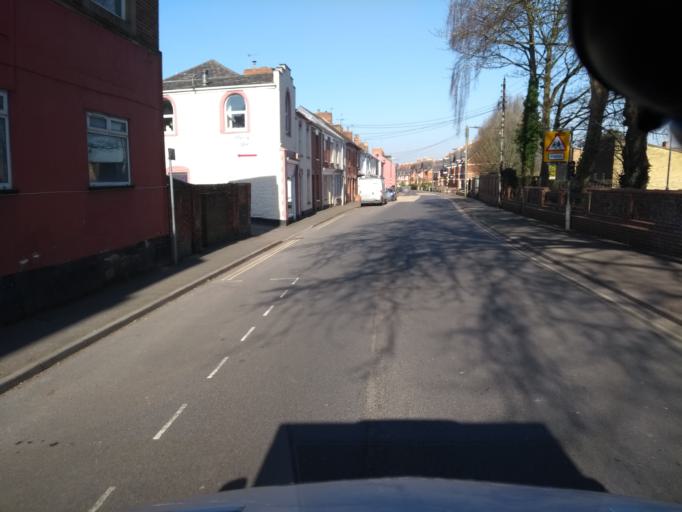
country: GB
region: England
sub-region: Somerset
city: Bishops Lydeard
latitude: 50.9792
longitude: -3.2311
